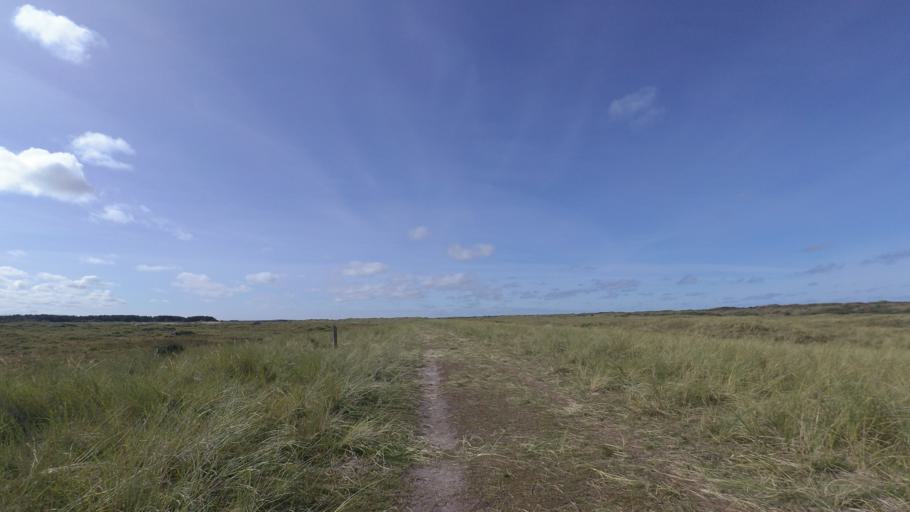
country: NL
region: Friesland
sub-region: Gemeente Ameland
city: Nes
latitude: 53.4541
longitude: 5.7100
